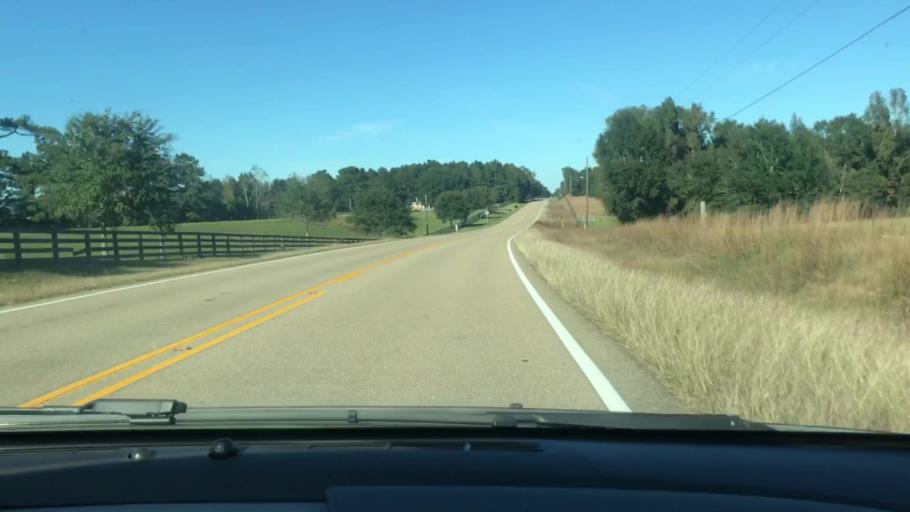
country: US
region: Louisiana
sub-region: Saint Tammany Parish
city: Abita Springs
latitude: 30.6036
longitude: -90.0291
